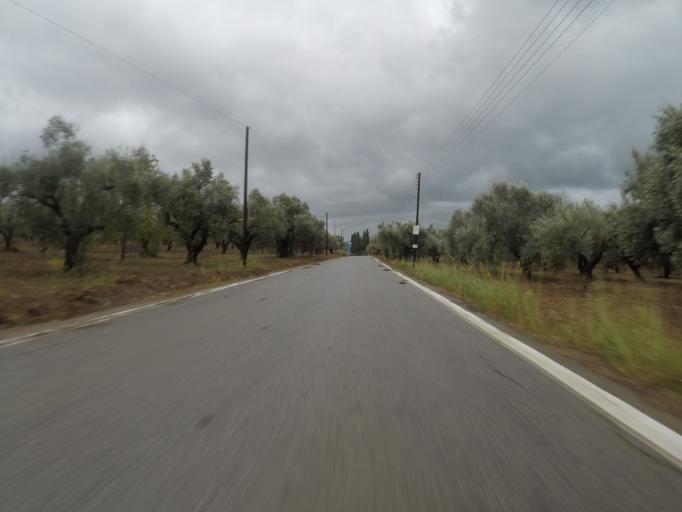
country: GR
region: Peloponnese
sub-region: Nomos Messinias
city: Pylos
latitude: 36.9770
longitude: 21.6862
